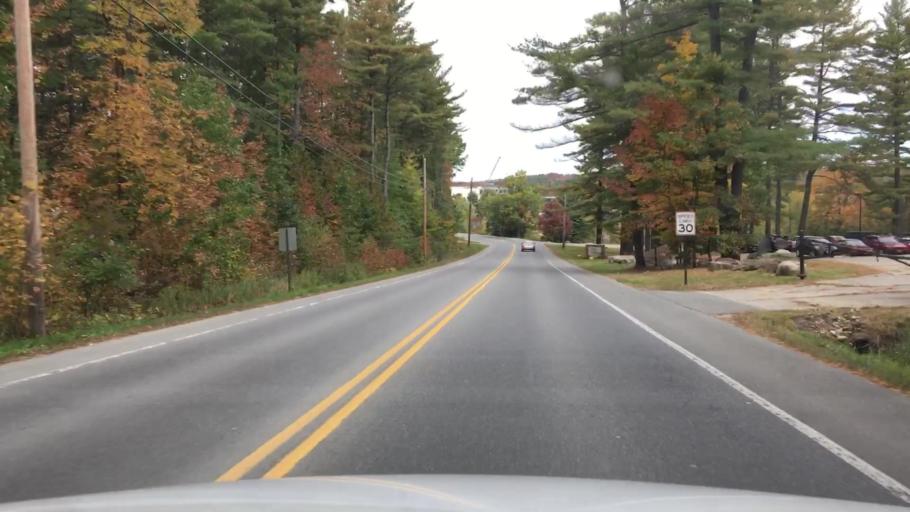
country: US
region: Maine
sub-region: Kennebec County
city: Waterville
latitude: 44.5625
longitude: -69.6677
